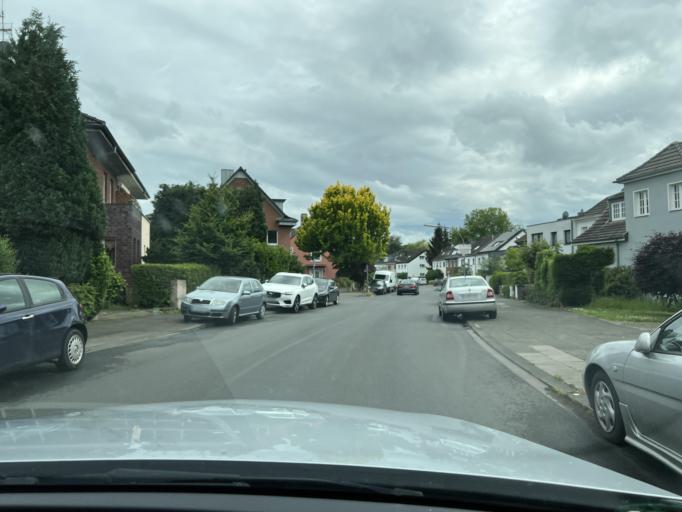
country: DE
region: North Rhine-Westphalia
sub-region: Regierungsbezirk Koln
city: Merheim
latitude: 50.9713
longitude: 7.0703
